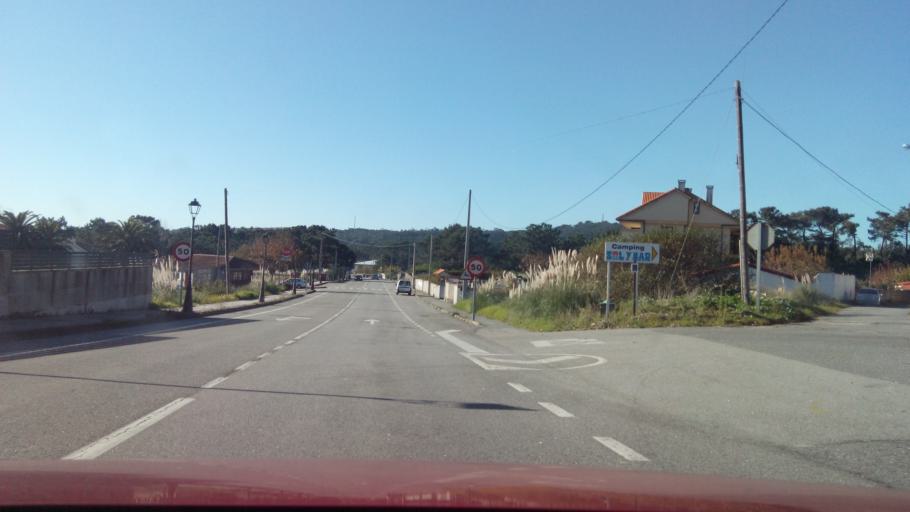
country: ES
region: Galicia
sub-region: Provincia de Pontevedra
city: O Grove
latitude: 42.4650
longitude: -8.9066
